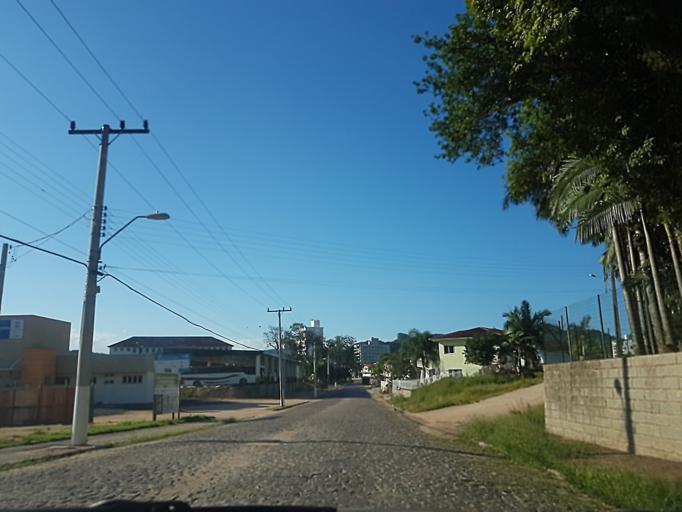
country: BR
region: Santa Catarina
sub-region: Braco Do Norte
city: Braco do Norte
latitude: -28.3296
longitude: -49.1729
